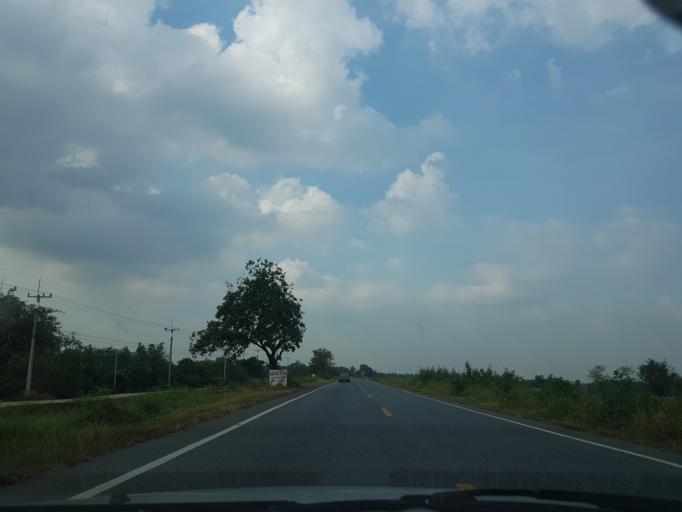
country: TH
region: Phra Nakhon Si Ayutthaya
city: Phachi
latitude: 14.4835
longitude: 100.7398
